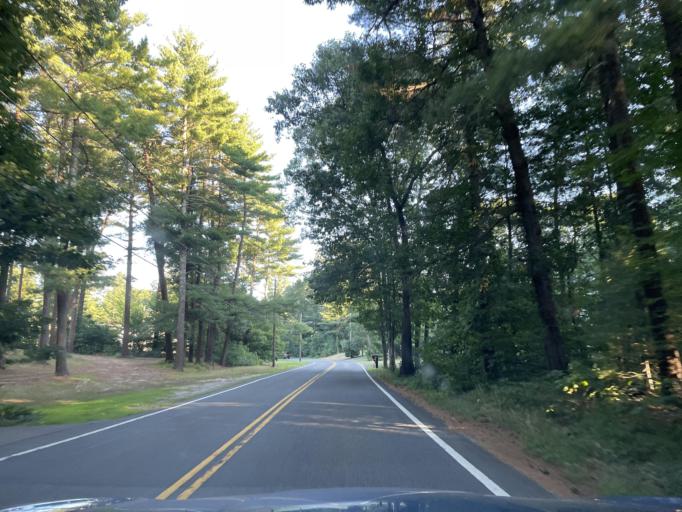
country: US
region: Massachusetts
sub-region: Plymouth County
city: East Bridgewater
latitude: 42.0088
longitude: -70.9573
